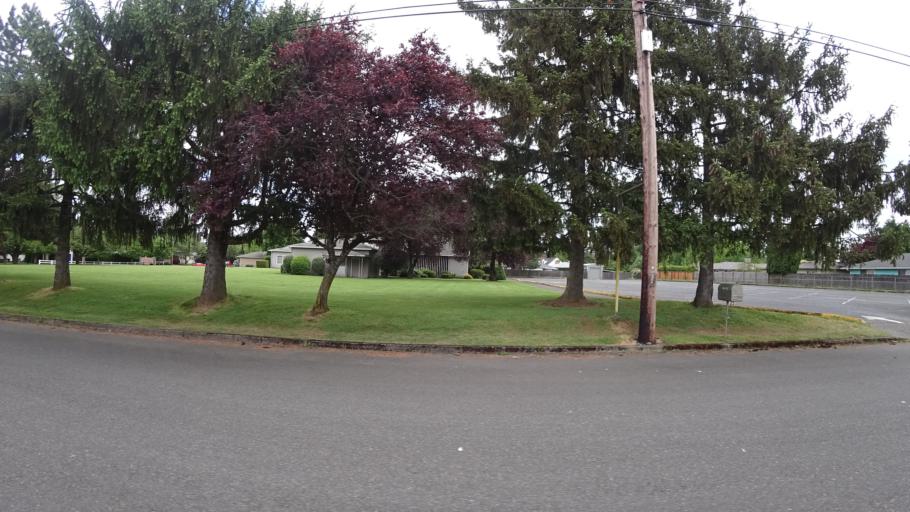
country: US
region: Oregon
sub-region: Multnomah County
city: Lents
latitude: 45.5109
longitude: -122.5538
